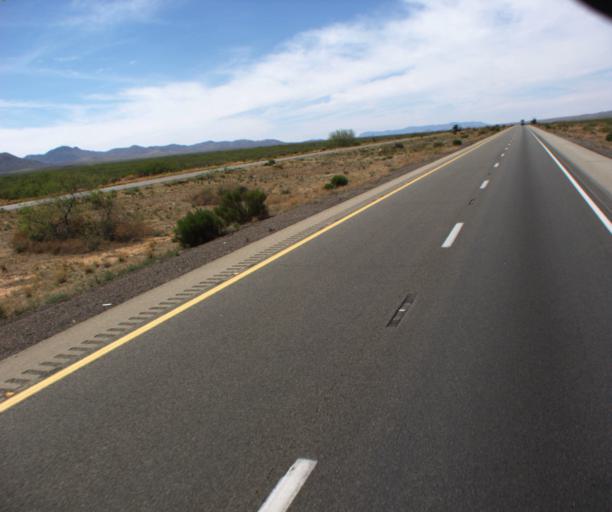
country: US
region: Arizona
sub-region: Cochise County
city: Willcox
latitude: 32.3388
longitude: -109.5530
